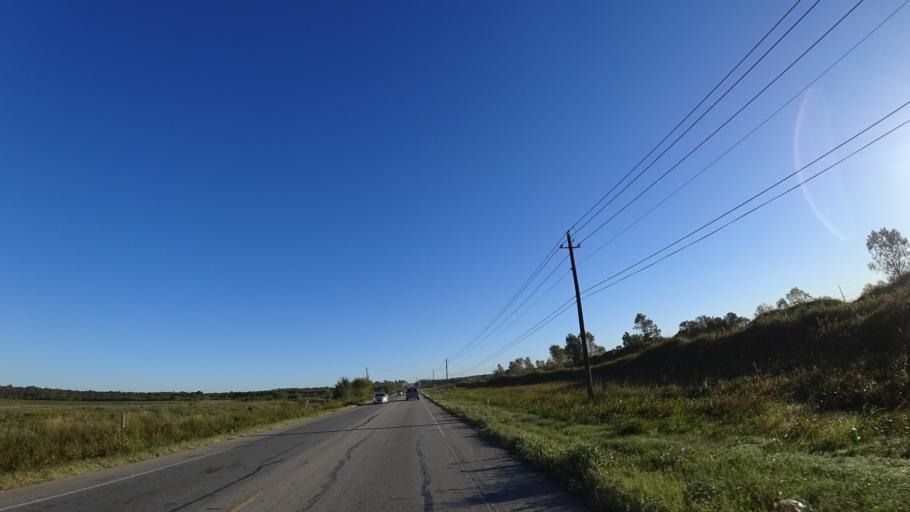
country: US
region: Texas
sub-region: Travis County
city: Hornsby Bend
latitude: 30.2502
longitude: -97.6162
